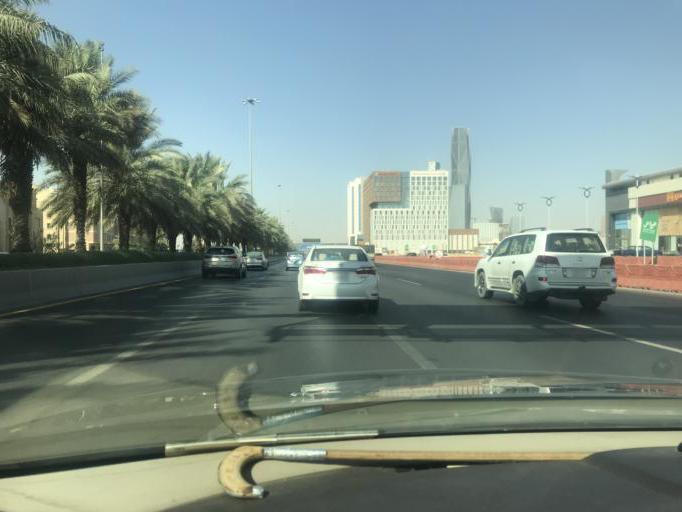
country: SA
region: Ar Riyad
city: Riyadh
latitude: 24.7658
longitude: 46.6593
